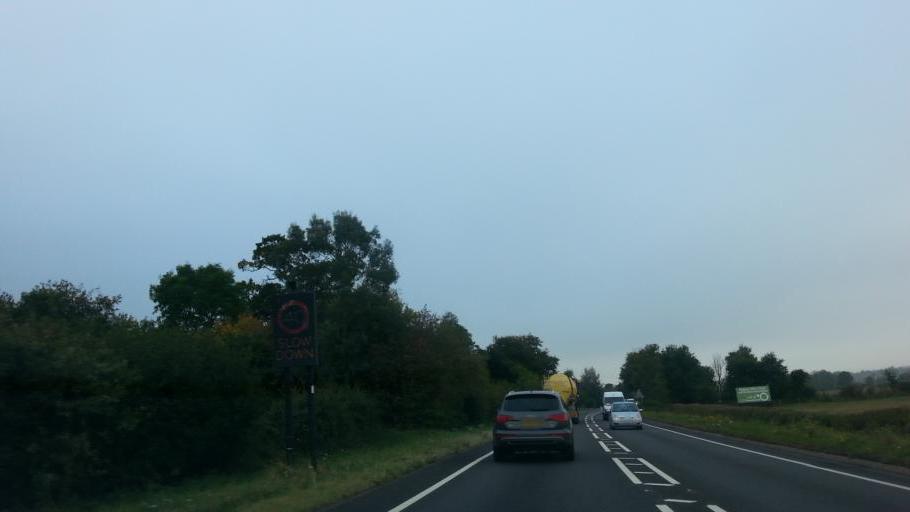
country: GB
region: England
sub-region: Northamptonshire
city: Oundle
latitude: 52.4953
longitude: -0.4493
